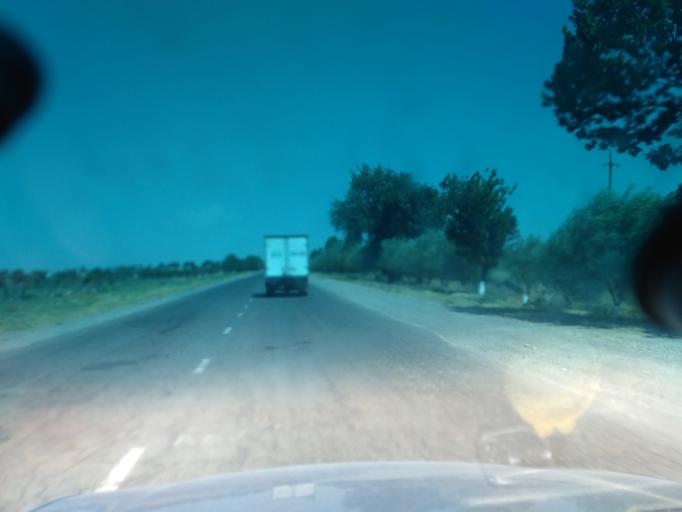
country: UZ
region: Sirdaryo
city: Guliston
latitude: 40.4868
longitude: 68.8916
